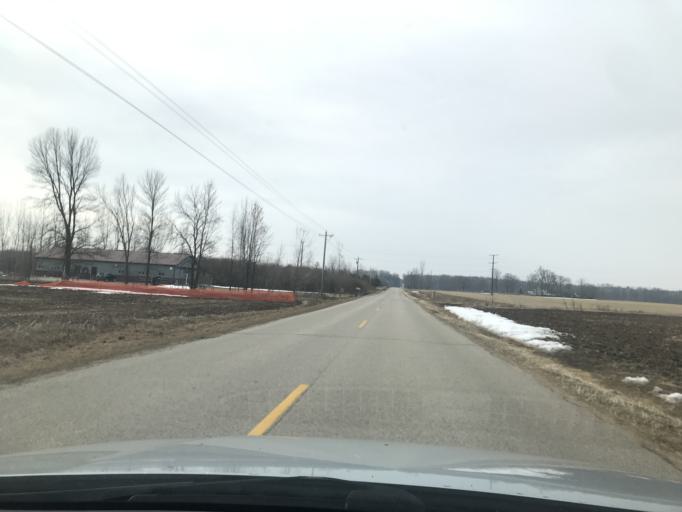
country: US
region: Wisconsin
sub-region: Oconto County
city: Oconto Falls
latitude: 44.8445
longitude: -88.1677
